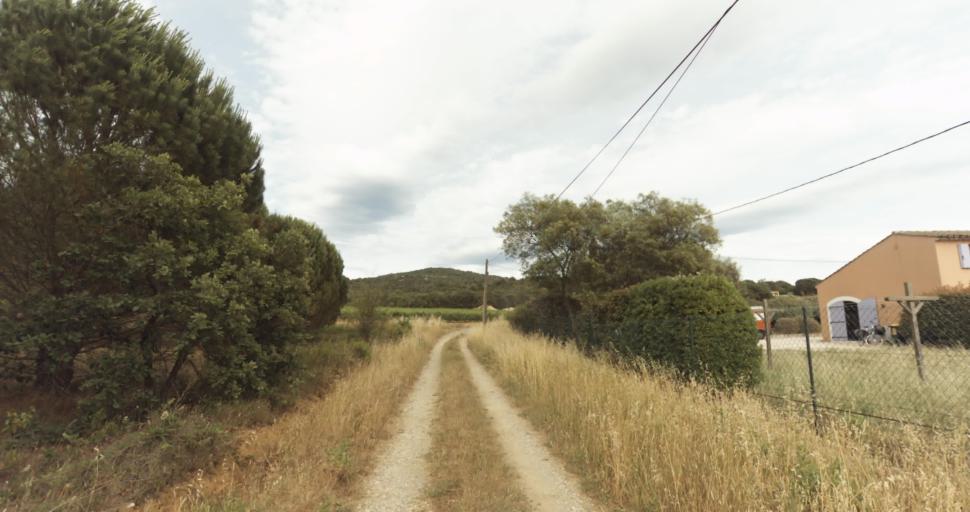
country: FR
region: Provence-Alpes-Cote d'Azur
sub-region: Departement du Var
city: Gassin
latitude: 43.2160
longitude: 6.5797
